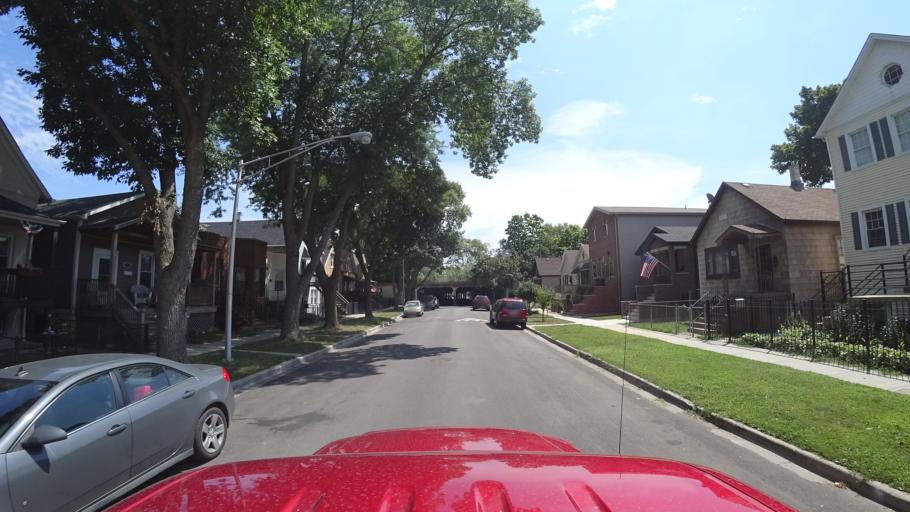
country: US
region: Illinois
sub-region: Cook County
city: Chicago
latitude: 41.8127
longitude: -87.6382
